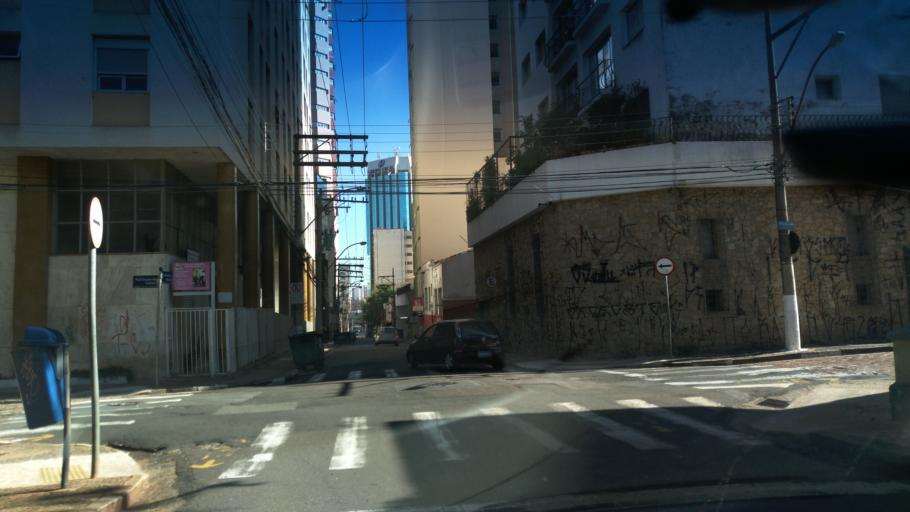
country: BR
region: Sao Paulo
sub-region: Campinas
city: Campinas
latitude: -22.9093
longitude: -47.0566
